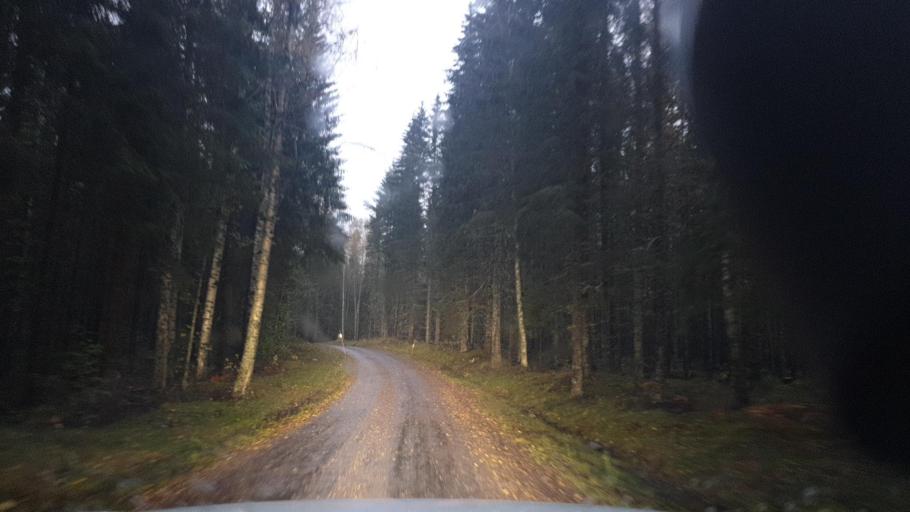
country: SE
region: Vaermland
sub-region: Eda Kommun
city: Amotfors
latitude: 59.8338
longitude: 12.3737
